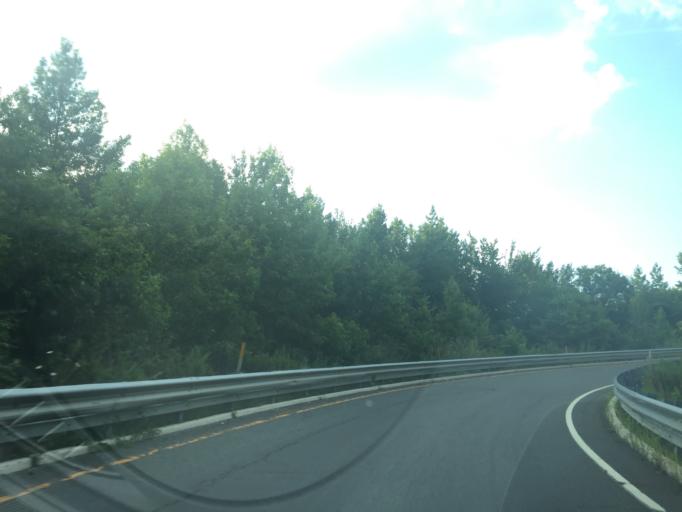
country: US
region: New Jersey
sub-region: Mercer County
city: Hightstown
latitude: 40.2814
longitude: -74.5319
